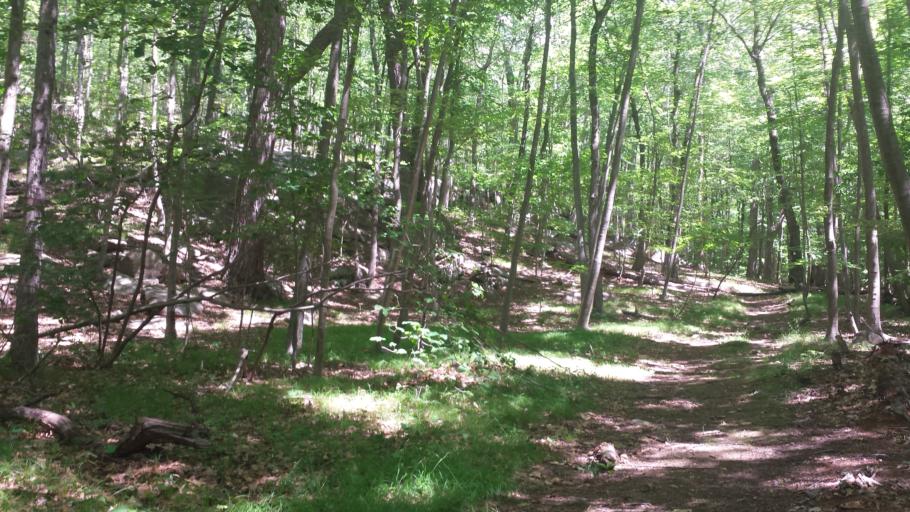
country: US
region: New York
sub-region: Westchester County
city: Pound Ridge
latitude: 41.2510
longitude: -73.5790
